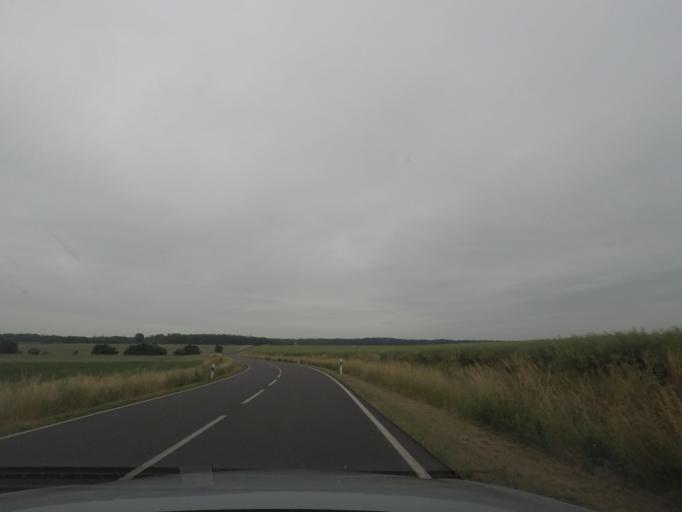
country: DE
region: Saxony-Anhalt
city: Seehausen
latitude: 52.0863
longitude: 11.2855
